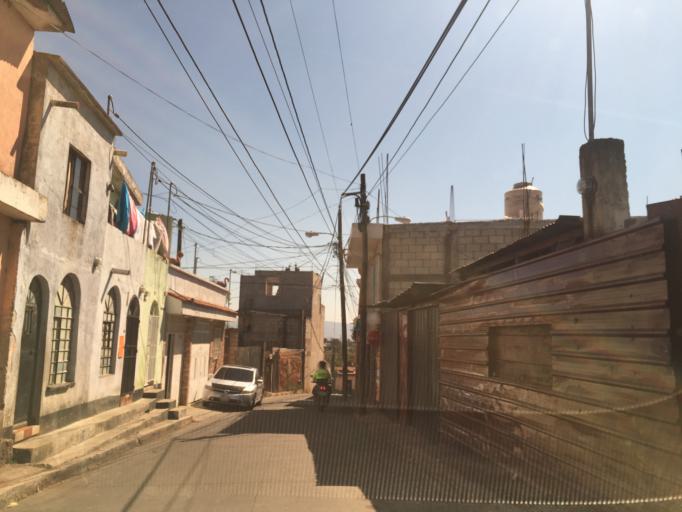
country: GT
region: Guatemala
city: Mixco
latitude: 14.6119
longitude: -90.5789
